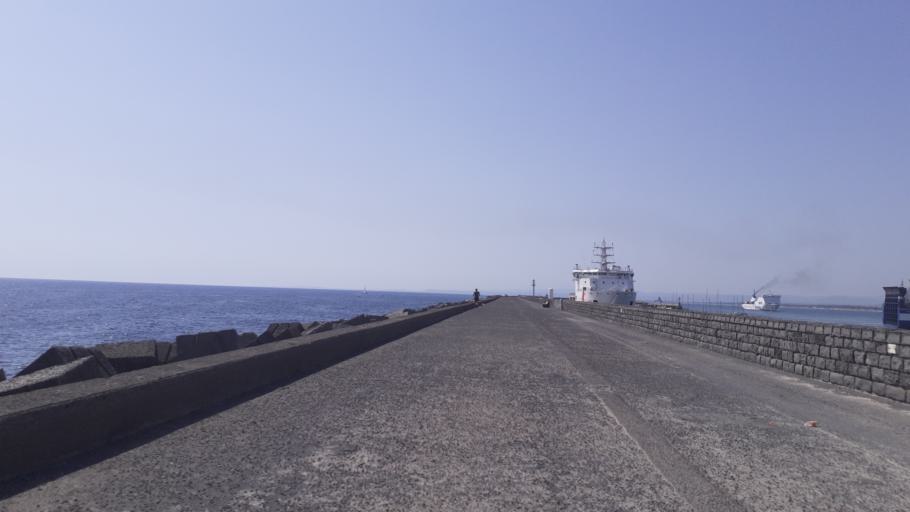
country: IT
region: Sicily
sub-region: Catania
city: Catania
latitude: 37.4963
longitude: 15.0995
